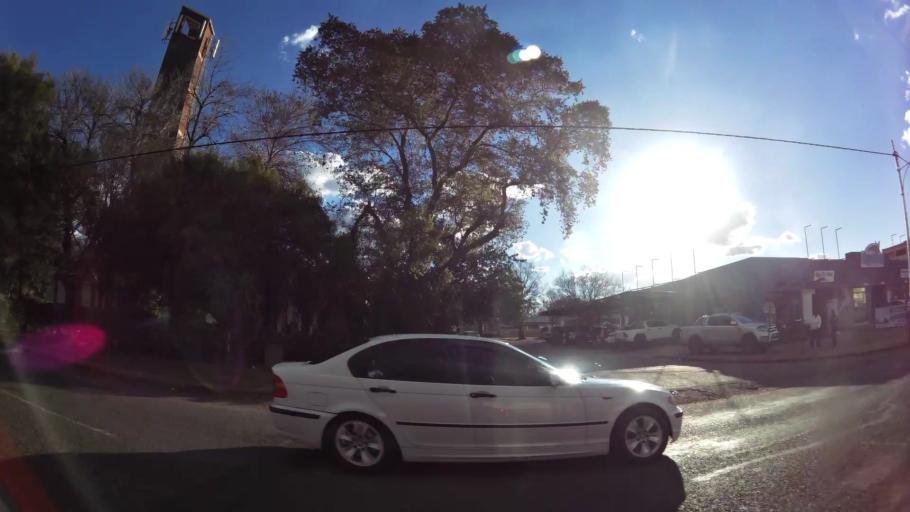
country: ZA
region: North-West
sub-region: Dr Kenneth Kaunda District Municipality
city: Potchefstroom
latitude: -26.7058
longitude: 27.0978
